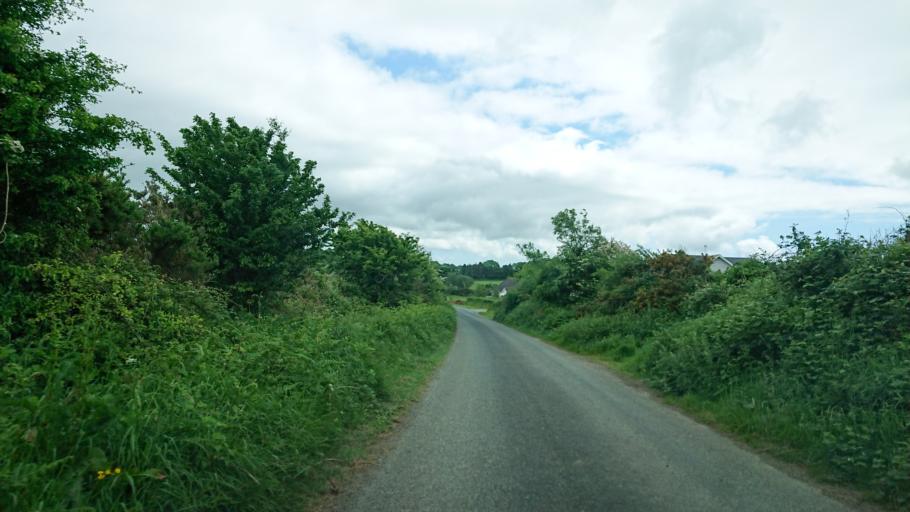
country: IE
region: Munster
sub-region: Waterford
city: Dunmore East
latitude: 52.2420
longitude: -7.0119
